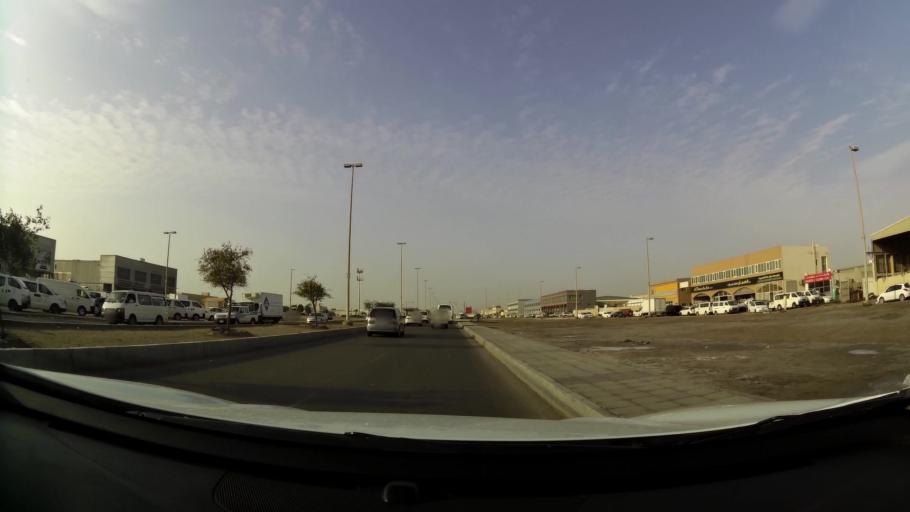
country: AE
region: Abu Dhabi
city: Abu Dhabi
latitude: 24.3478
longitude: 54.5172
